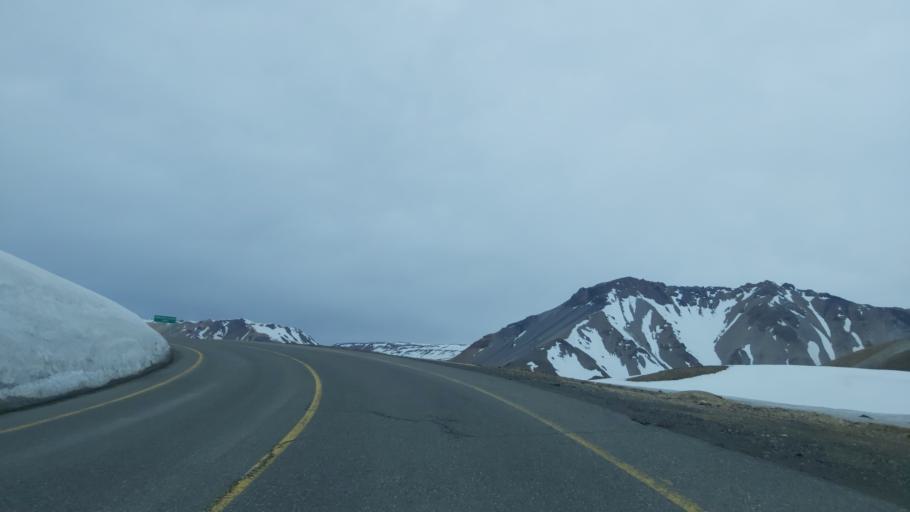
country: CL
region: Maule
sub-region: Provincia de Linares
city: Colbun
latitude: -36.0126
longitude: -70.4851
